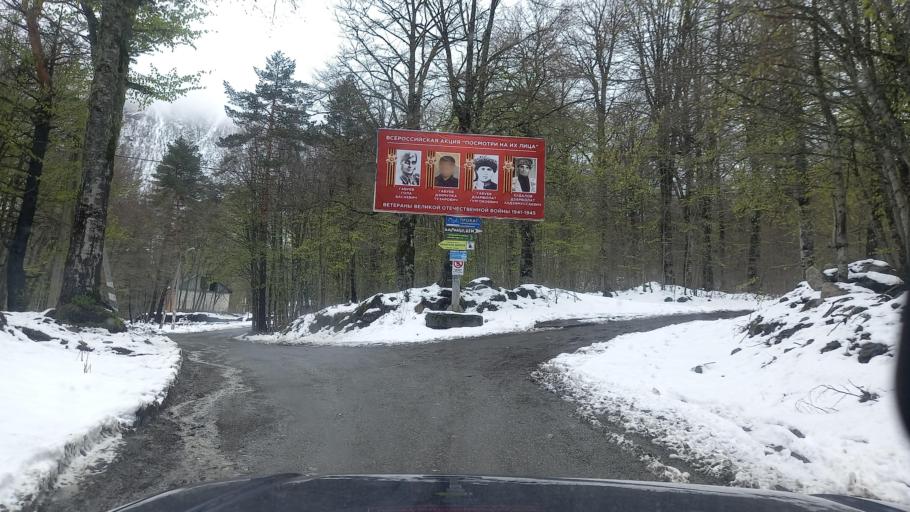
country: RU
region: North Ossetia
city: Mizur
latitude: 42.7884
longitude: 43.9026
